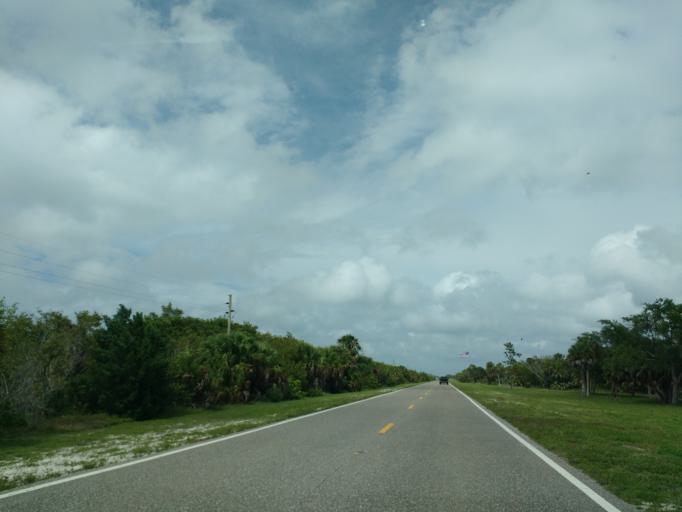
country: US
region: Florida
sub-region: Pinellas County
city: Tierra Verde
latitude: 27.6198
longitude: -82.7227
